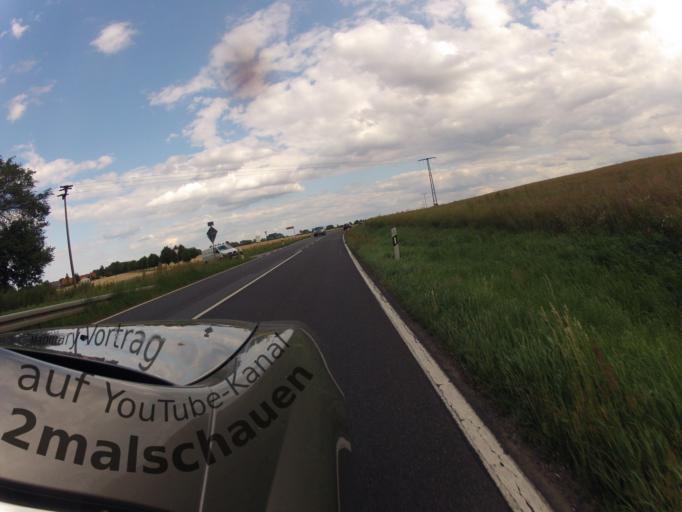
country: DE
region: Mecklenburg-Vorpommern
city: Seebad Bansin
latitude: 53.8978
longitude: 14.0628
